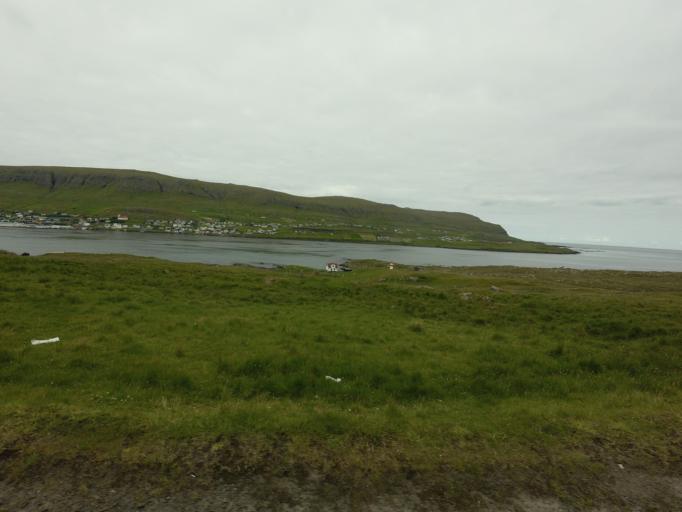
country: FO
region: Suduroy
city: Tvoroyri
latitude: 61.5420
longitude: -6.8062
